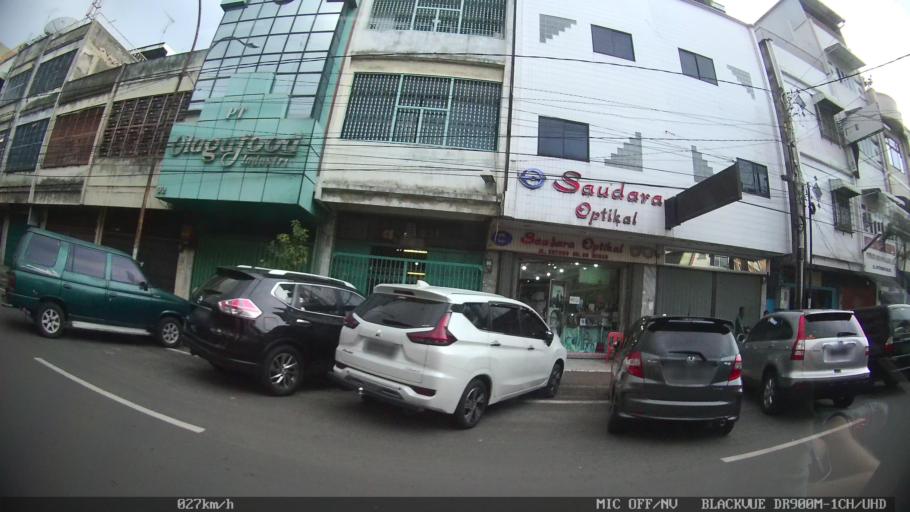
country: ID
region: North Sumatra
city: Medan
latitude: 3.5819
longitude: 98.6881
